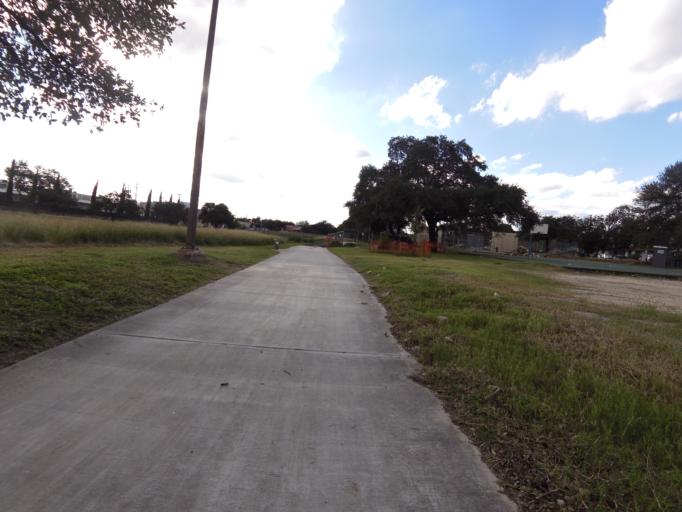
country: US
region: Texas
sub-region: Bexar County
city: San Antonio
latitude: 29.4138
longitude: -98.5270
